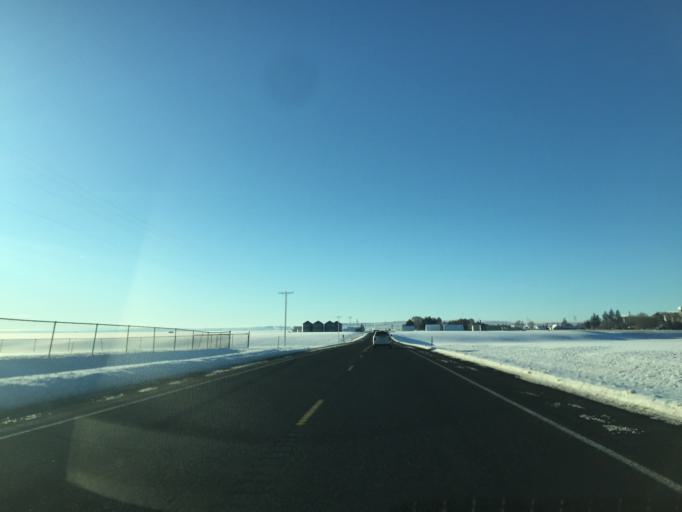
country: US
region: Washington
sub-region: Okanogan County
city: Coulee Dam
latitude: 47.6848
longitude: -119.0958
